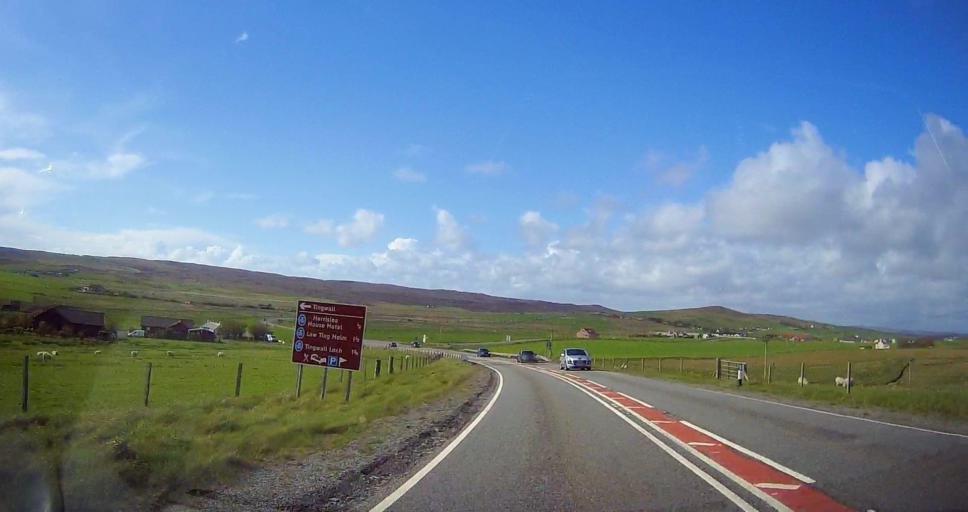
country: GB
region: Scotland
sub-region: Shetland Islands
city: Lerwick
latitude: 60.1841
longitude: -1.2245
